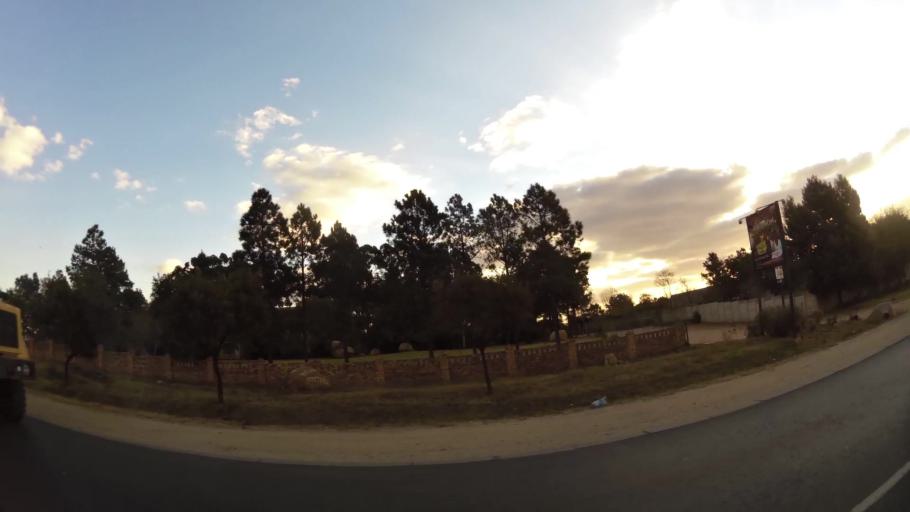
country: ZA
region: Gauteng
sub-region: City of Johannesburg Metropolitan Municipality
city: Midrand
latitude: -26.0000
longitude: 28.1564
